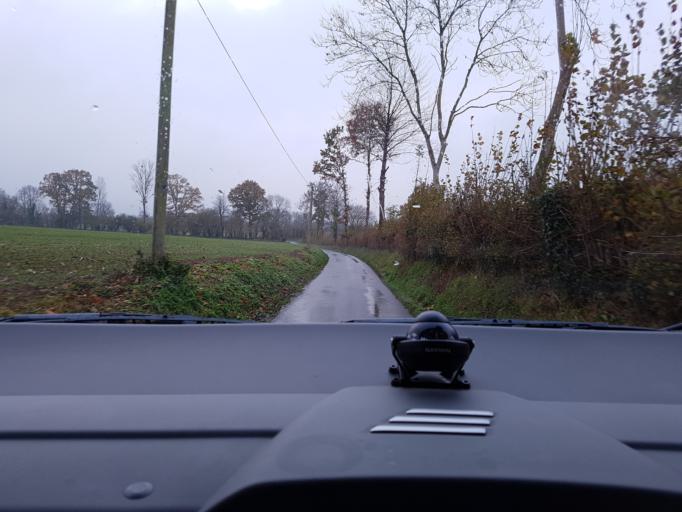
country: FR
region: Haute-Normandie
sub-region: Departement de l'Eure
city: Beuzeville
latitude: 49.3584
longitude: 0.3752
